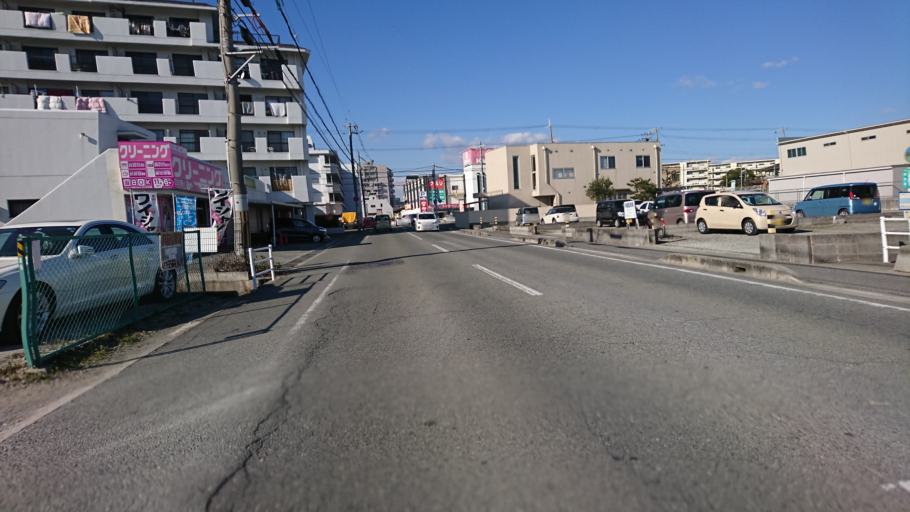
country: JP
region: Hyogo
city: Kakogawacho-honmachi
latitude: 34.7380
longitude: 134.8628
